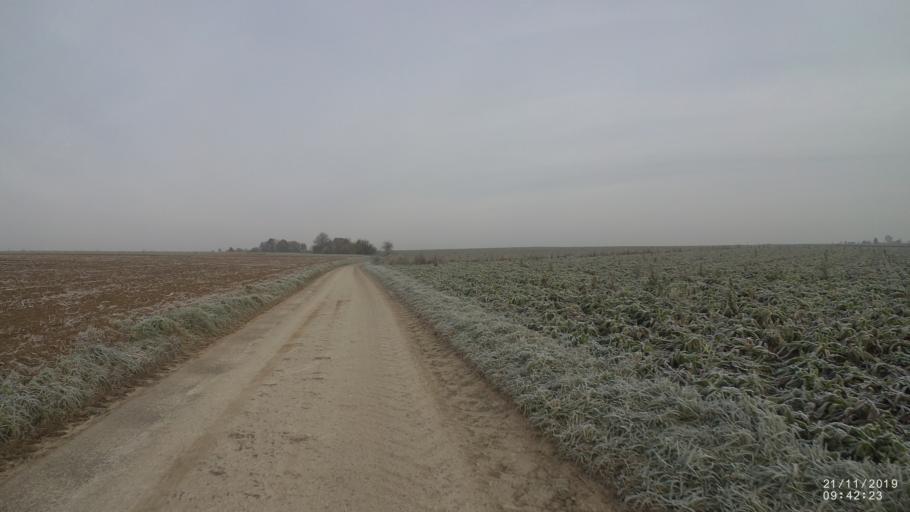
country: BE
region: Flanders
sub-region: Provincie Vlaams-Brabant
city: Tienen
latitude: 50.7812
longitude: 4.9969
